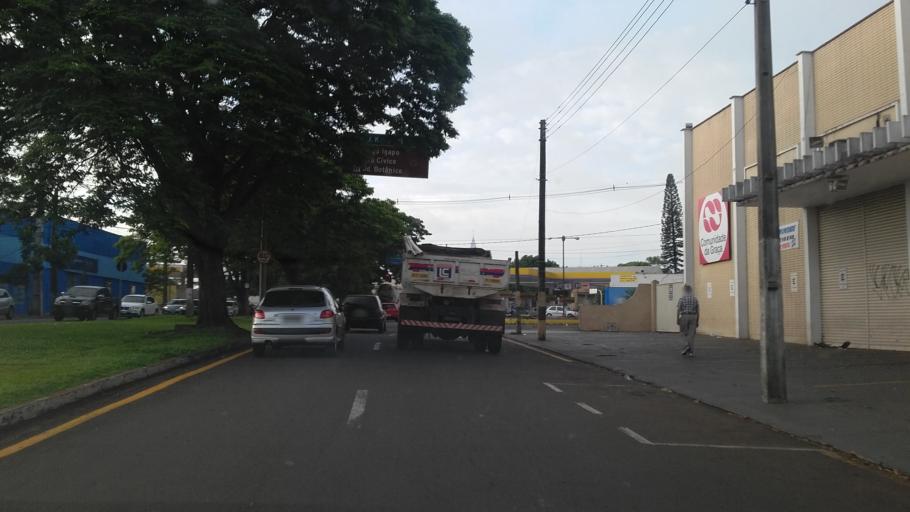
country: BR
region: Parana
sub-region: Londrina
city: Londrina
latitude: -23.3006
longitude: -51.1736
